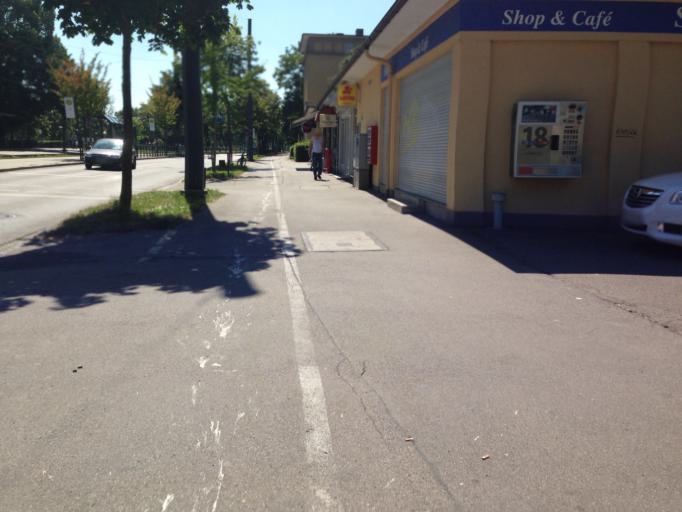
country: DE
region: Bavaria
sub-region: Swabia
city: Augsburg
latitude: 48.3488
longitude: 10.9005
